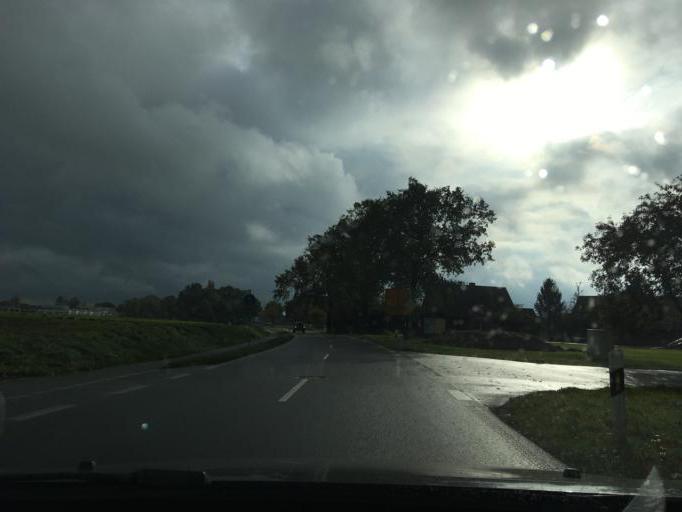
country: DE
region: North Rhine-Westphalia
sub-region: Regierungsbezirk Munster
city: Vreden
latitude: 52.0499
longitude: 6.8058
